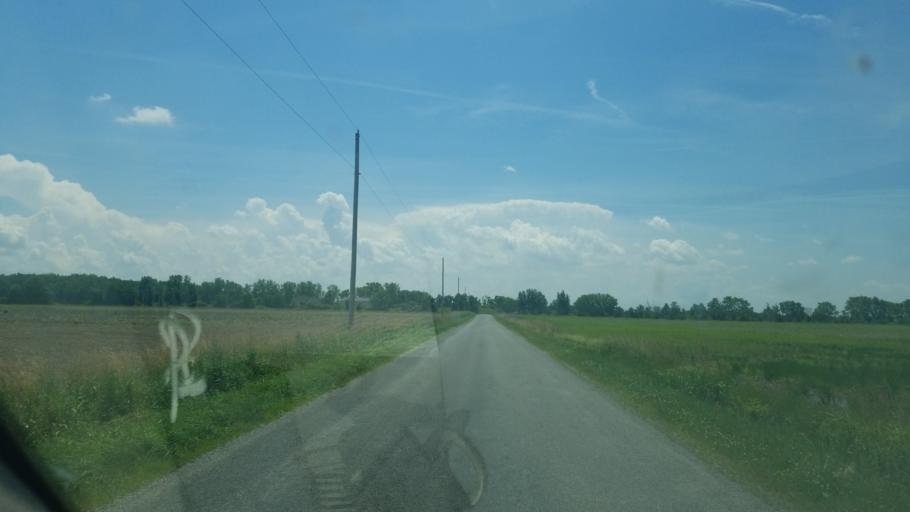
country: US
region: Ohio
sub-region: Hancock County
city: Findlay
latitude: 40.9968
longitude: -83.6362
